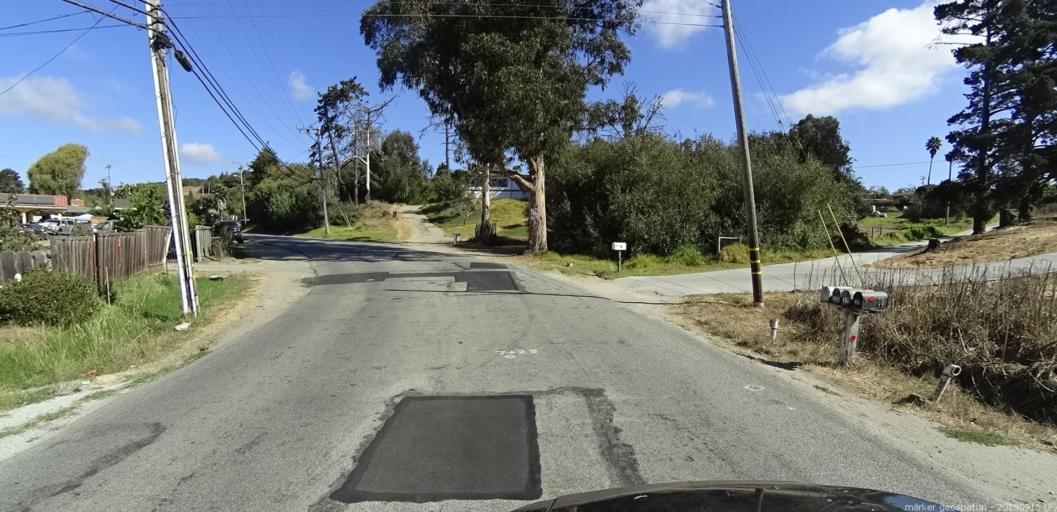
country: US
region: California
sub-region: Monterey County
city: Las Lomas
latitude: 36.8669
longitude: -121.7329
